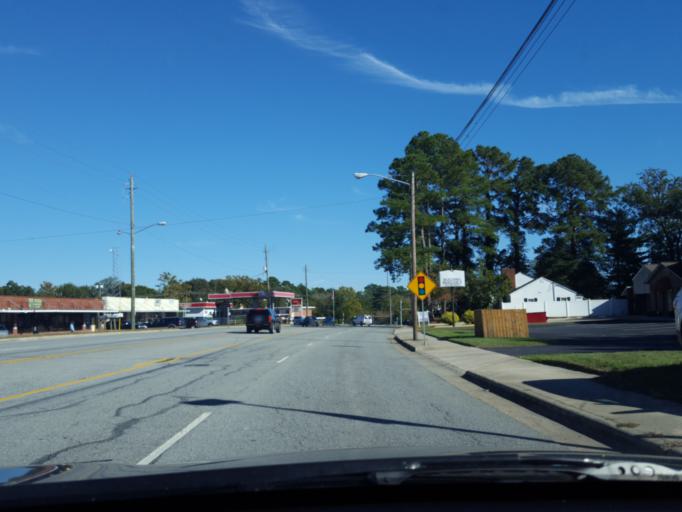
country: US
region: North Carolina
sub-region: Pitt County
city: Greenville
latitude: 35.6034
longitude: -77.3428
